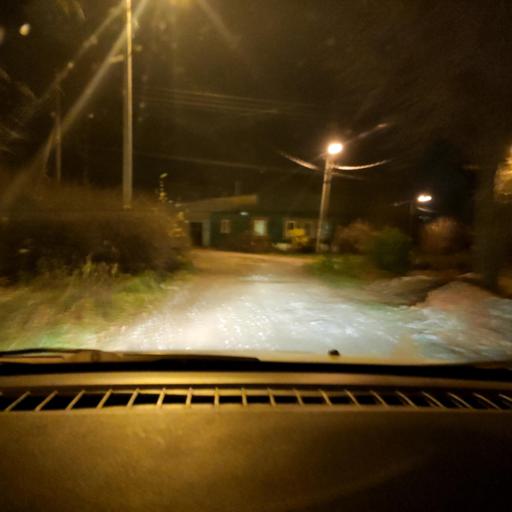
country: RU
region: Perm
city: Perm
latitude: 58.0439
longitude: 56.3414
